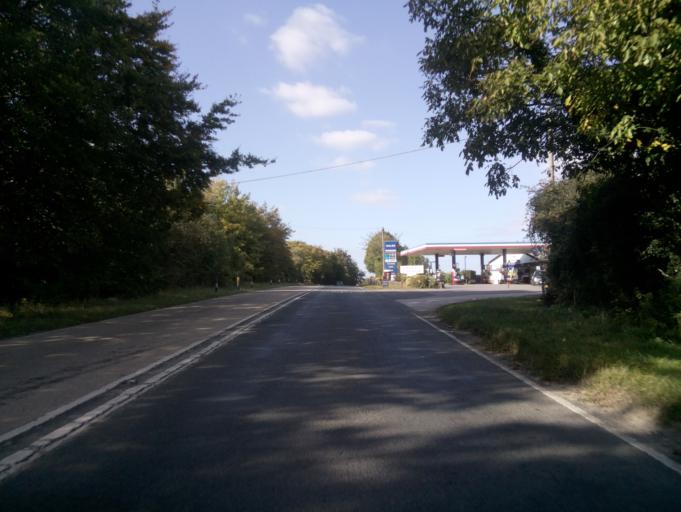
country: GB
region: England
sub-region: Hampshire
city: Basingstoke
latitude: 51.2887
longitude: -1.1163
